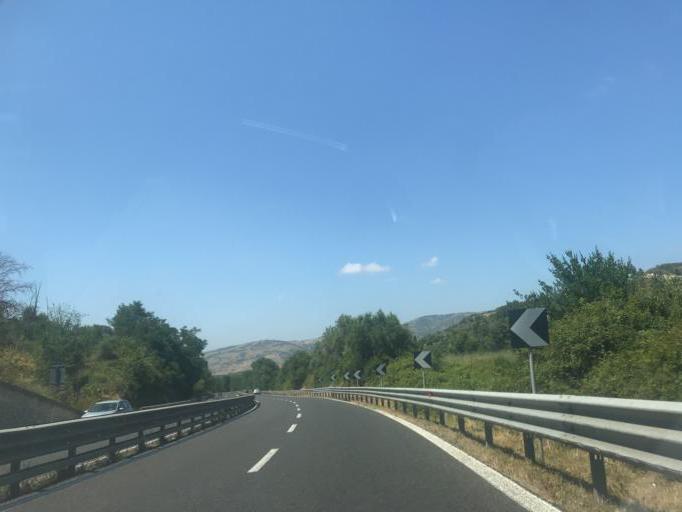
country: IT
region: Sardinia
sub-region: Provincia di Sassari
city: Codrongianos
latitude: 40.6585
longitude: 8.6715
